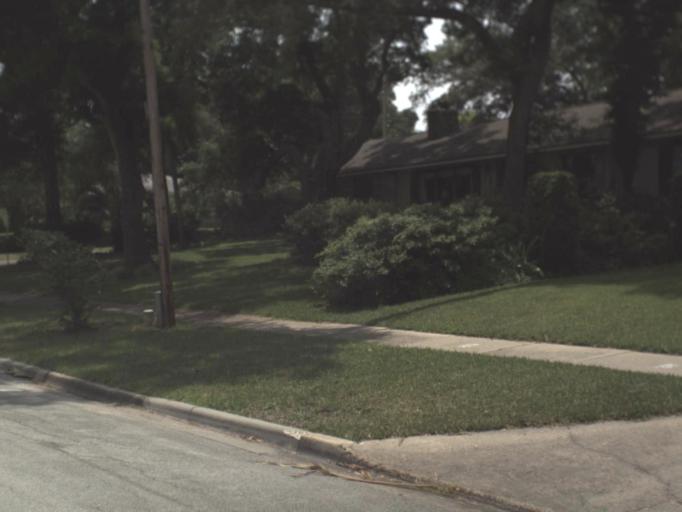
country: US
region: Florida
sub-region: Nassau County
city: Fernandina Beach
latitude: 30.6690
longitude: -81.4439
